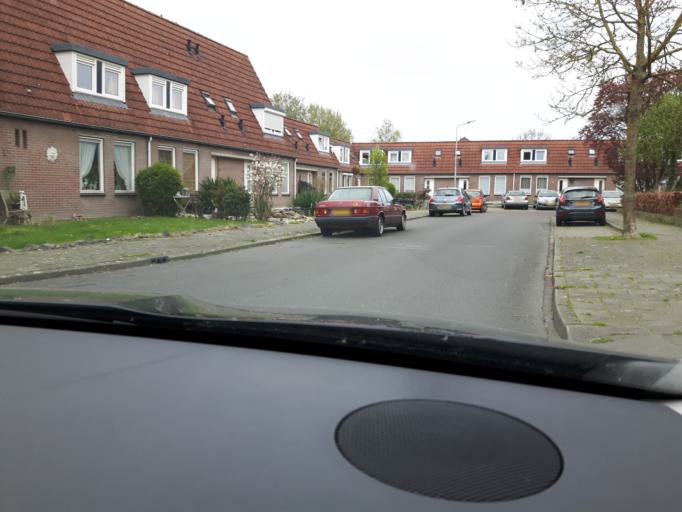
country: NL
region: Zeeland
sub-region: Gemeente Goes
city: Goes
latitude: 51.4886
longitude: 3.9592
